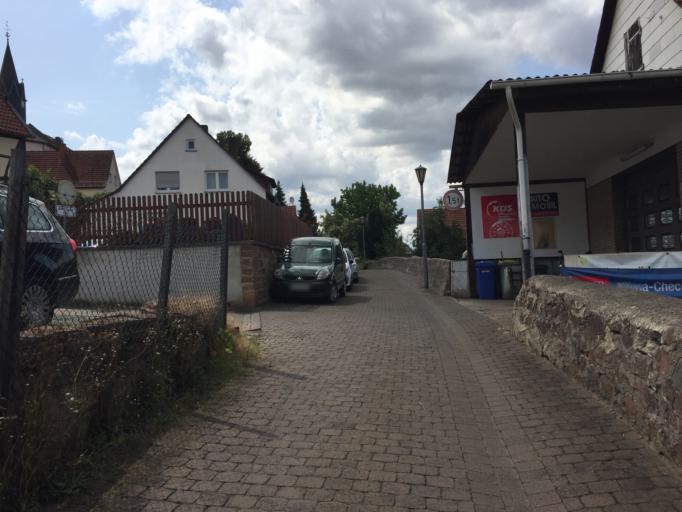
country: DE
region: Hesse
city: Schwalmstadt
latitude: 50.9141
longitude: 9.1864
